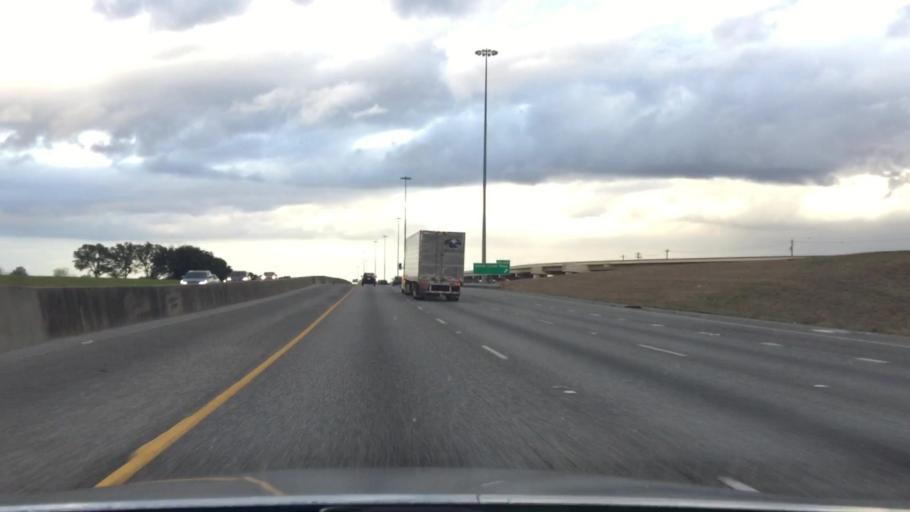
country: US
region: Texas
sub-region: Travis County
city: Onion Creek
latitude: 30.1130
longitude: -97.8071
